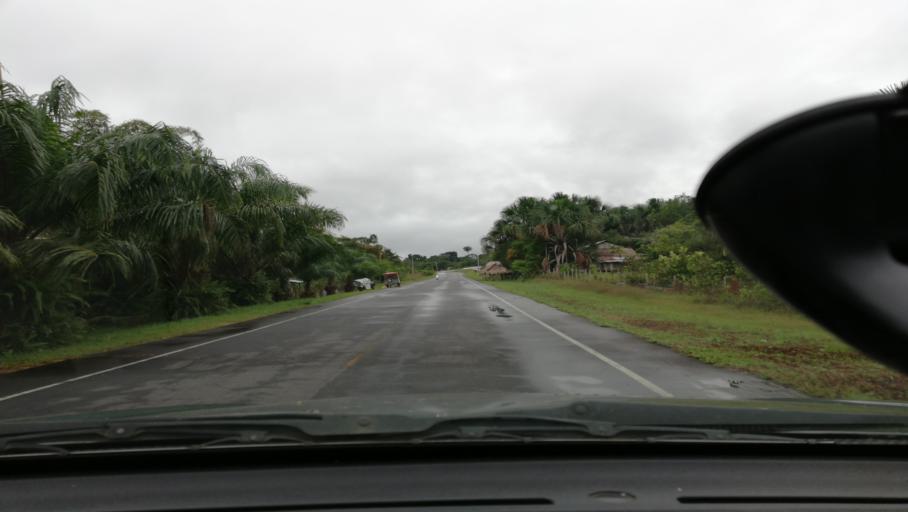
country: PE
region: Loreto
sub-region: Provincia de Loreto
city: Nauta
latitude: -4.3544
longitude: -73.5495
